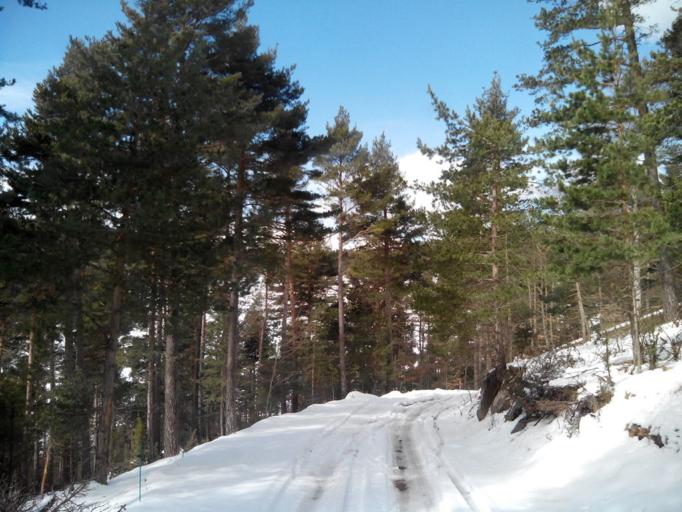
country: ES
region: Catalonia
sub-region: Provincia de Barcelona
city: Sant Julia de Cerdanyola
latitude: 42.1950
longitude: 1.9270
